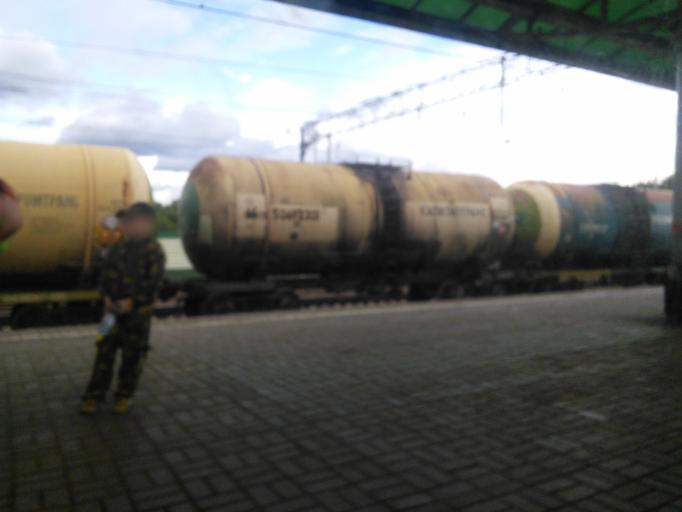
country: RU
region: Moskovskaya
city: Lyubertsy
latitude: 55.6816
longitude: 37.8984
